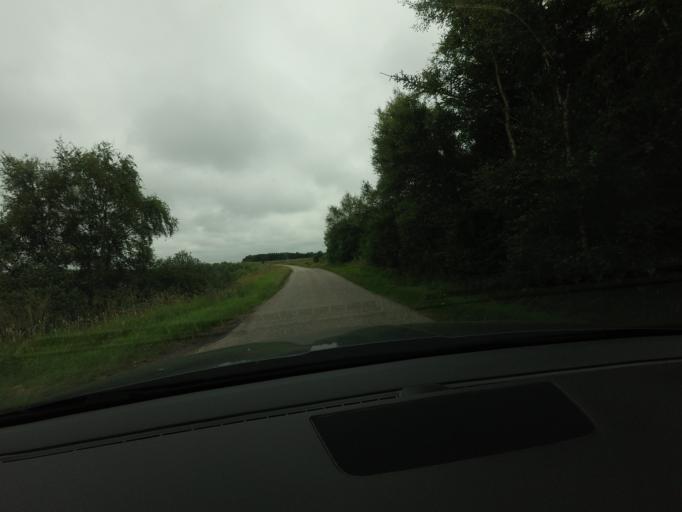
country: GB
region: Scotland
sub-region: Highland
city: Alness
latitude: 58.0747
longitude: -4.4122
